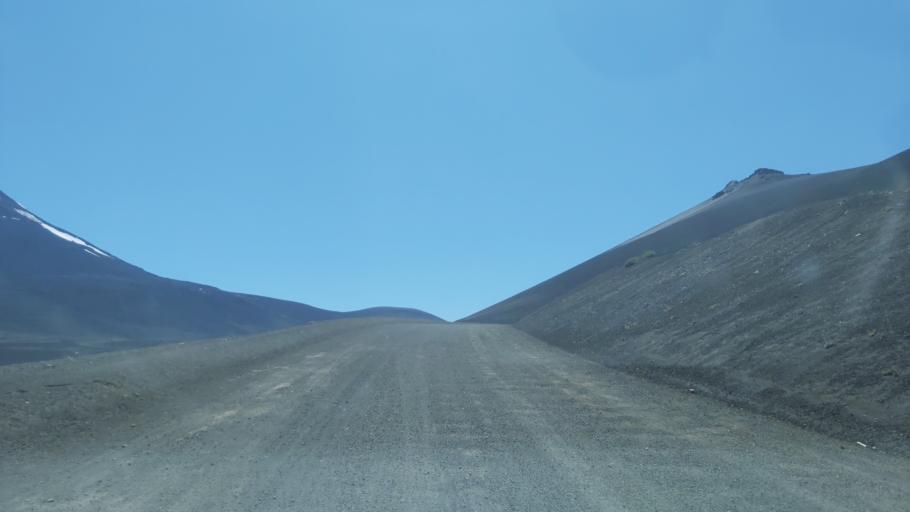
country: CL
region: Araucania
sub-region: Provincia de Cautin
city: Vilcun
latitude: -38.4114
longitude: -71.5421
